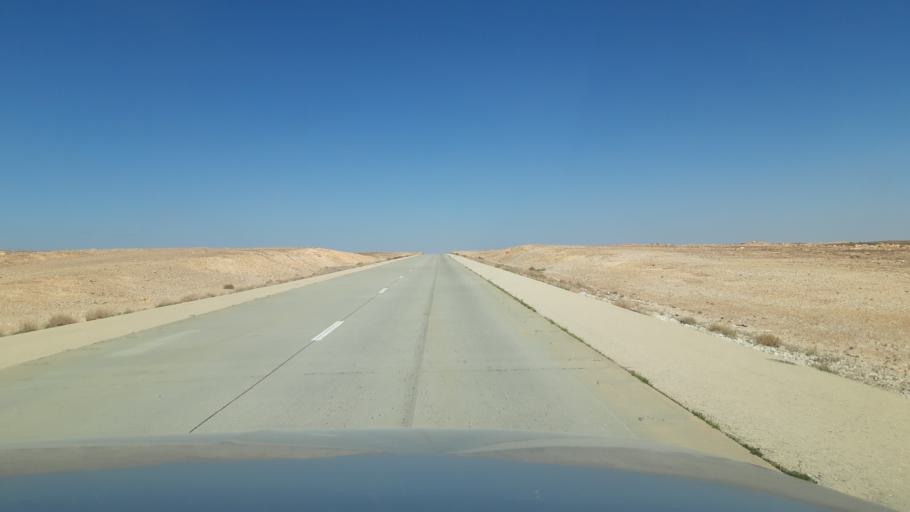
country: SA
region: Al Jawf
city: Al Qurayyat
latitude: 31.0925
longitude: 36.6351
